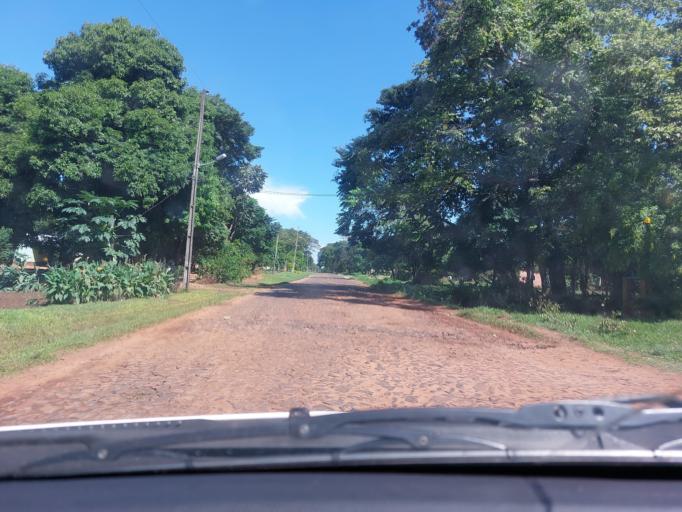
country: PY
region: San Pedro
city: Itacurubi del Rosario
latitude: -24.5701
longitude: -56.5962
